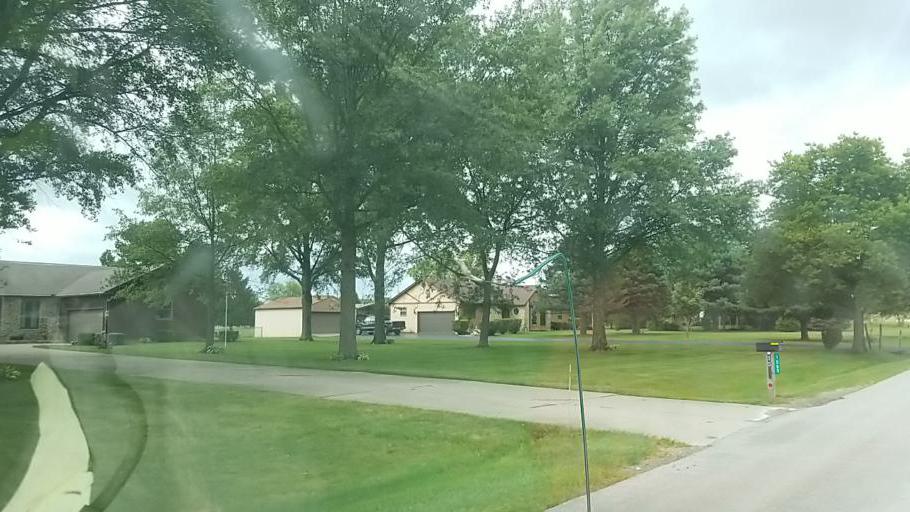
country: US
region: Ohio
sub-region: Pickaway County
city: Commercial Point
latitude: 39.8266
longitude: -83.0462
